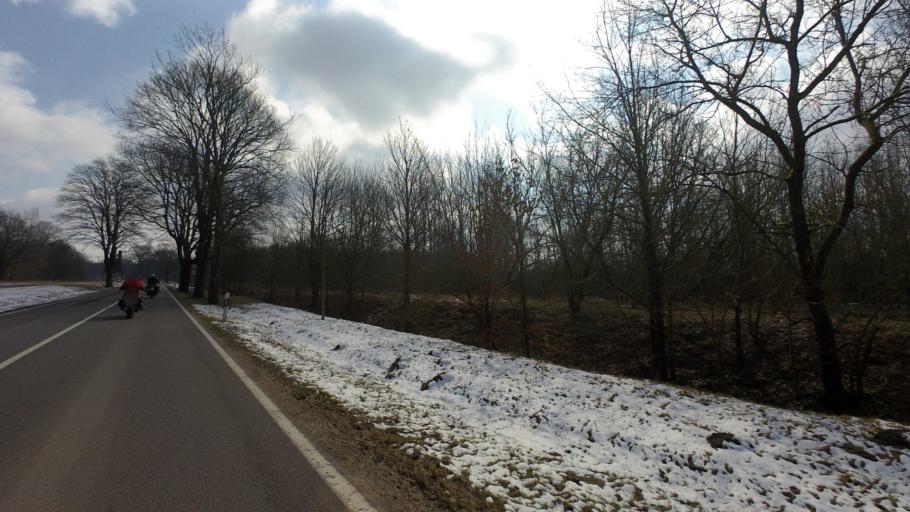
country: DE
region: Berlin
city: Buch
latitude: 52.6770
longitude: 13.5053
